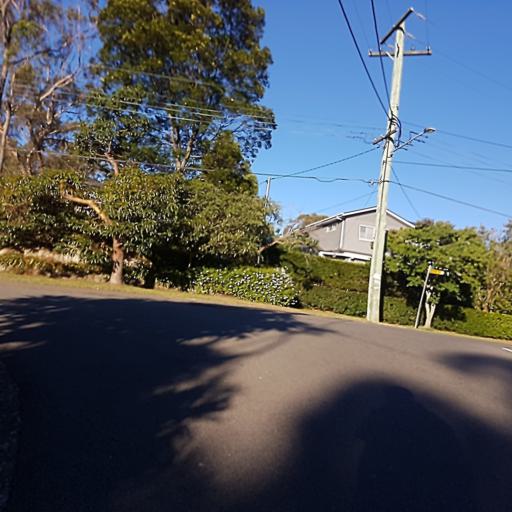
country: AU
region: New South Wales
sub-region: Warringah
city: Forestville
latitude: -33.7551
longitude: 151.2195
